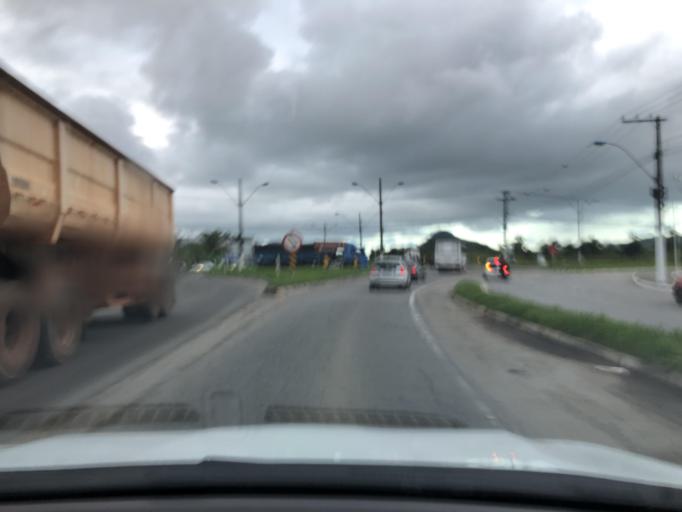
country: BR
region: Santa Catarina
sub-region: Sao Francisco Do Sul
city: Sao Francisco do Sul
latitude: -26.2525
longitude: -48.6184
